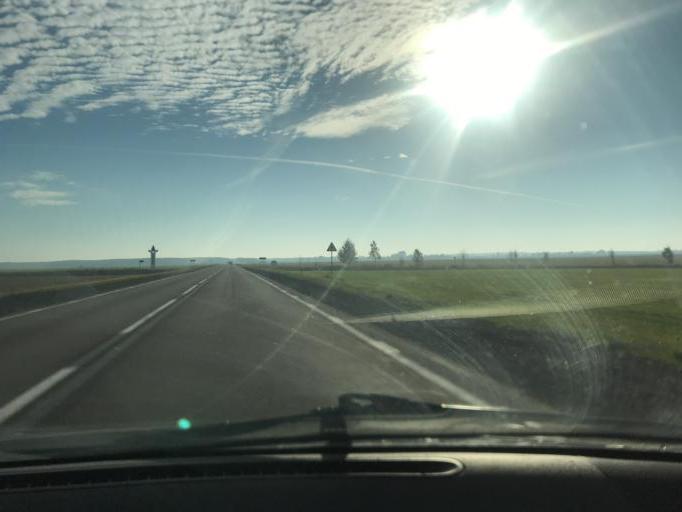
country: BY
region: Brest
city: Drahichyn
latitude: 52.1927
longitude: 25.2555
